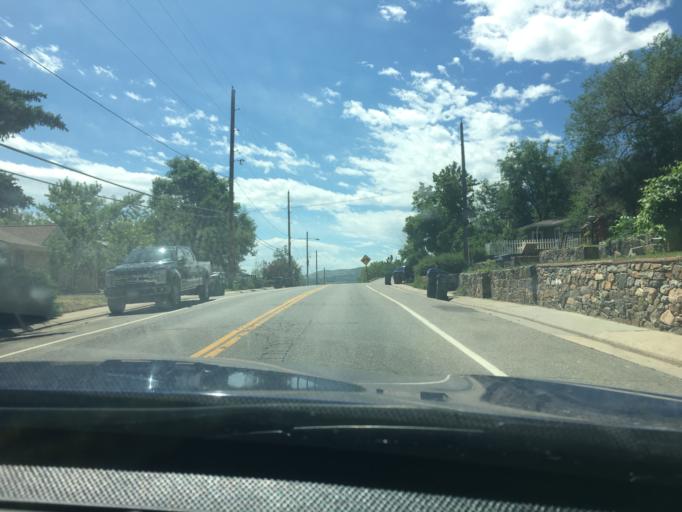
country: US
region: Colorado
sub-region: Jefferson County
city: Golden
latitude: 39.7648
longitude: -105.2269
